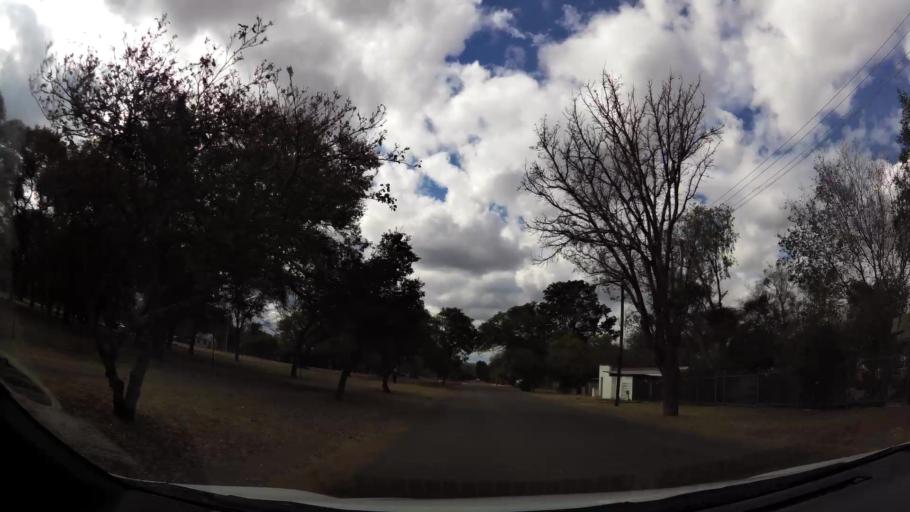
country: ZA
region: Limpopo
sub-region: Waterberg District Municipality
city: Modimolle
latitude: -24.7067
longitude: 28.4007
